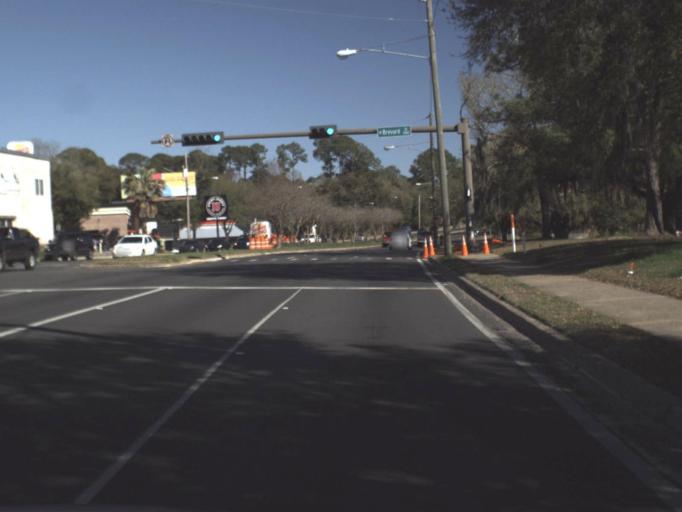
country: US
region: Florida
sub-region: Leon County
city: Tallahassee
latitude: 30.4488
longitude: -84.3045
